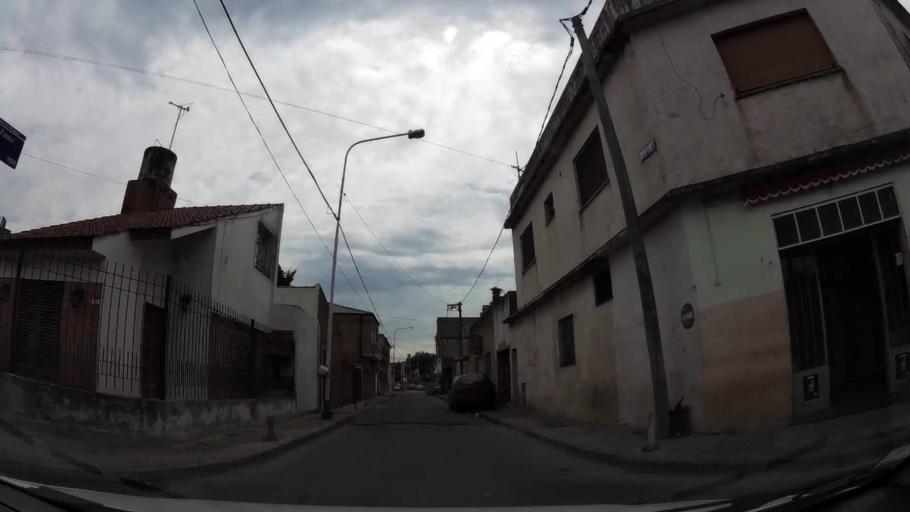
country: AR
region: Buenos Aires F.D.
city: Villa Lugano
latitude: -34.6846
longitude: -58.5105
